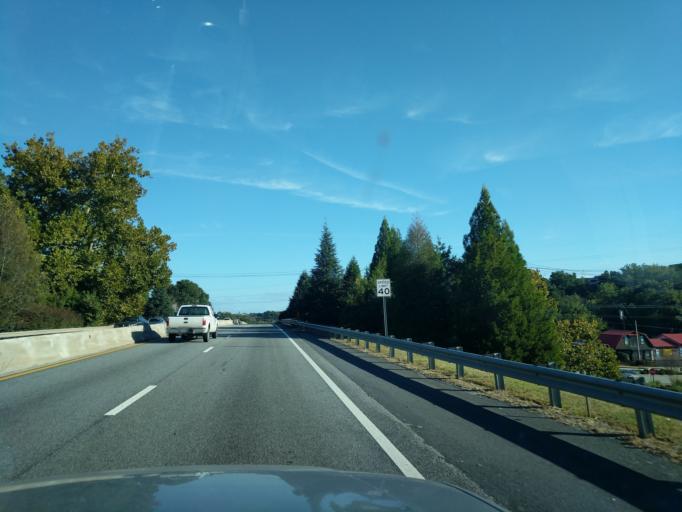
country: US
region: South Carolina
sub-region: Spartanburg County
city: Spartanburg
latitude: 34.9733
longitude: -81.9394
